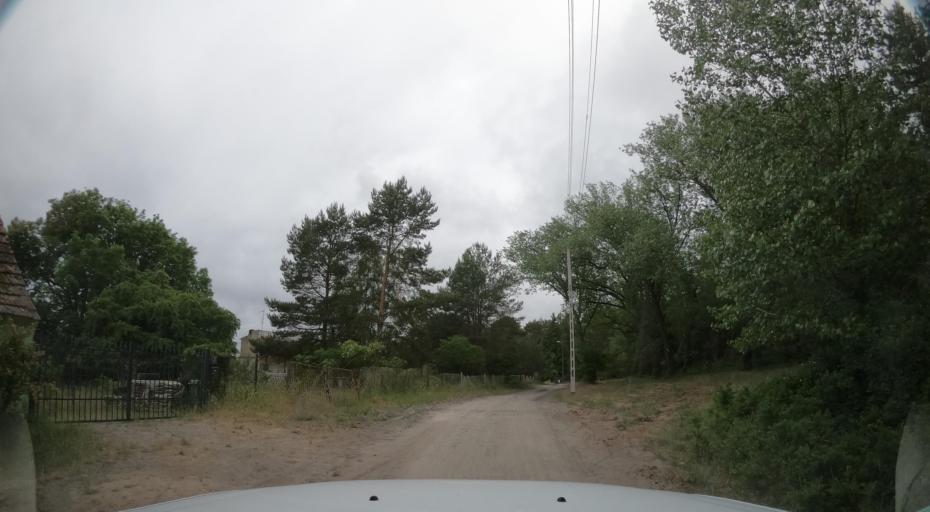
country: PL
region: West Pomeranian Voivodeship
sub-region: Powiat kamienski
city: Miedzyzdroje
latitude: 53.8605
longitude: 14.5166
